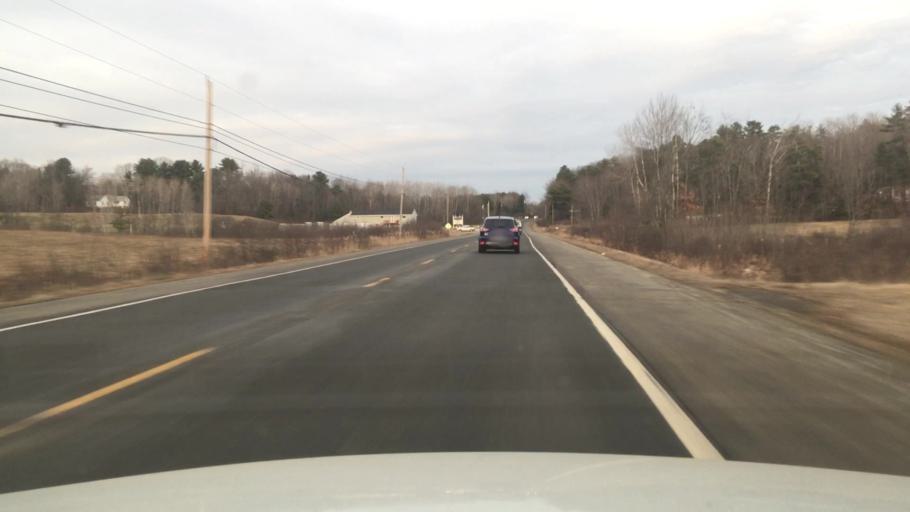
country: US
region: Maine
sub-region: Lincoln County
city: Damariscotta
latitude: 44.0168
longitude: -69.5826
